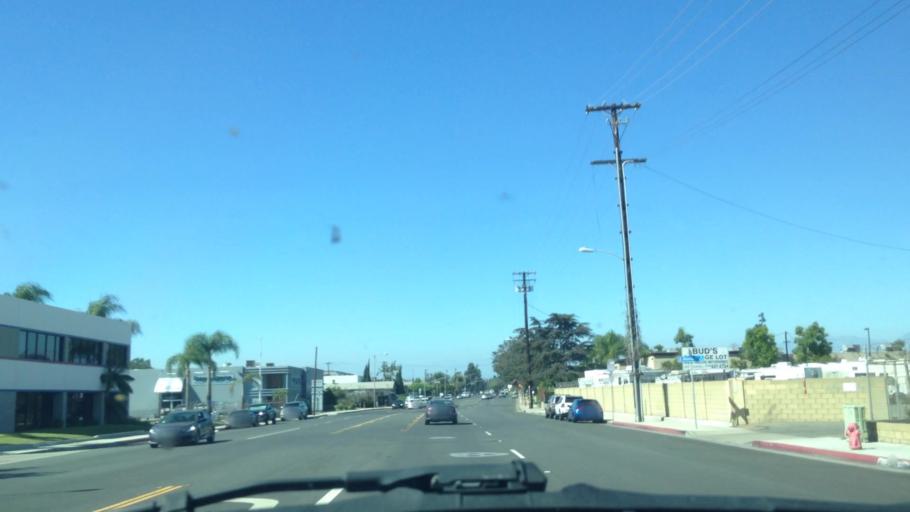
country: US
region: California
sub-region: Orange County
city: Orange
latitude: 33.8184
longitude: -117.8532
